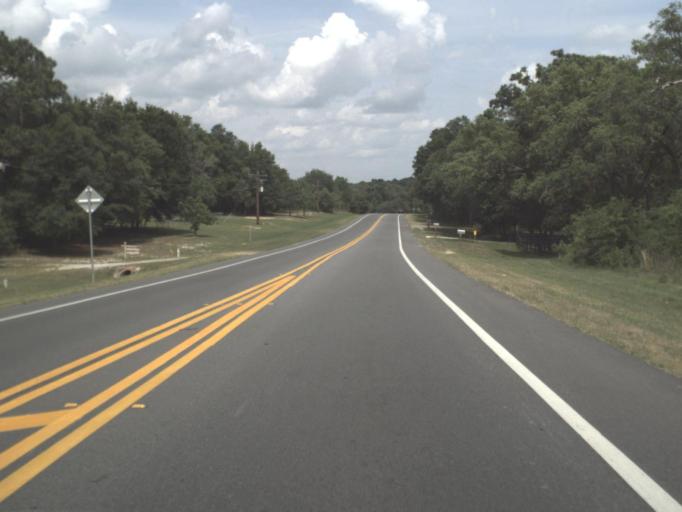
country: US
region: Florida
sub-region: Alachua County
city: Hawthorne
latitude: 29.6084
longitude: -82.0234
